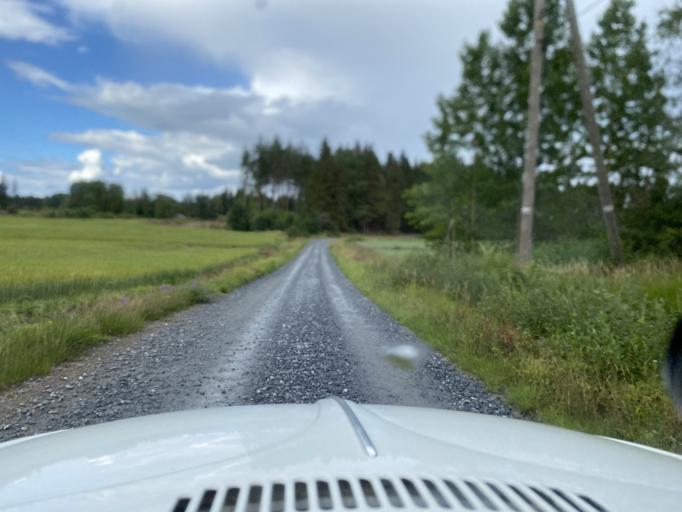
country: FI
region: Pirkanmaa
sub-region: Lounais-Pirkanmaa
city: Punkalaidun
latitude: 61.1287
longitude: 23.0648
